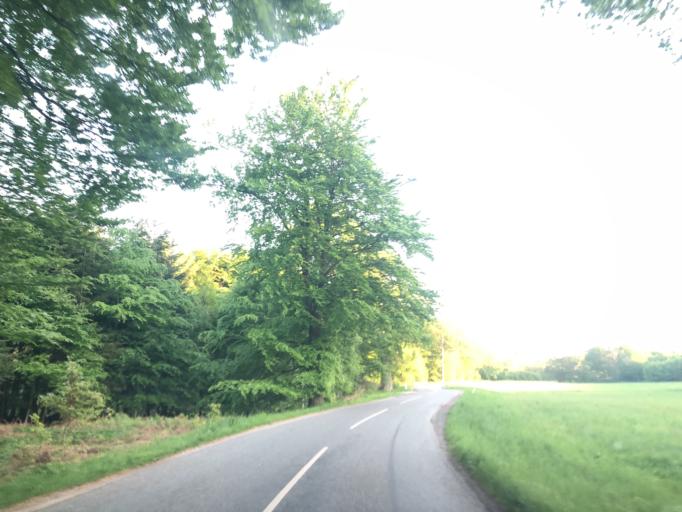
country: DK
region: Zealand
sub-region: Koge Kommune
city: Borup
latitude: 55.4267
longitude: 11.9394
